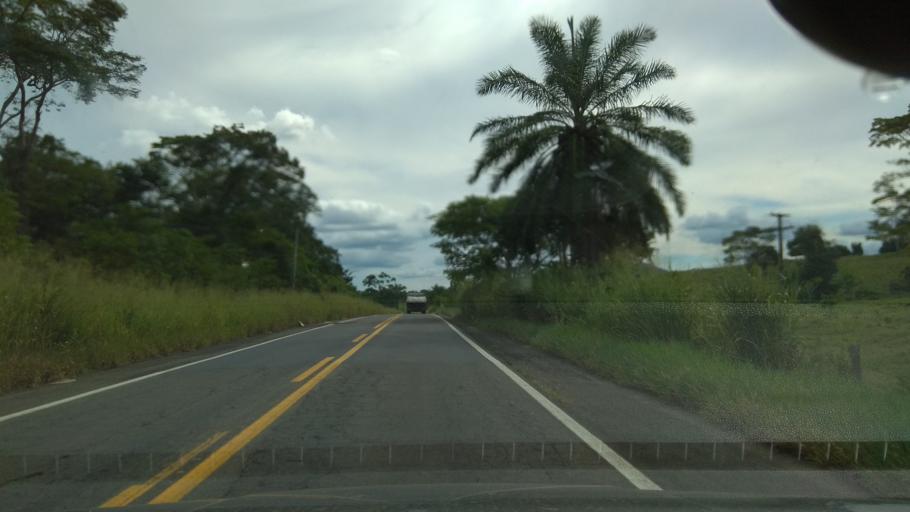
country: BR
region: Bahia
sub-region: Ipiau
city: Ipiau
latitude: -14.1942
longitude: -39.6457
